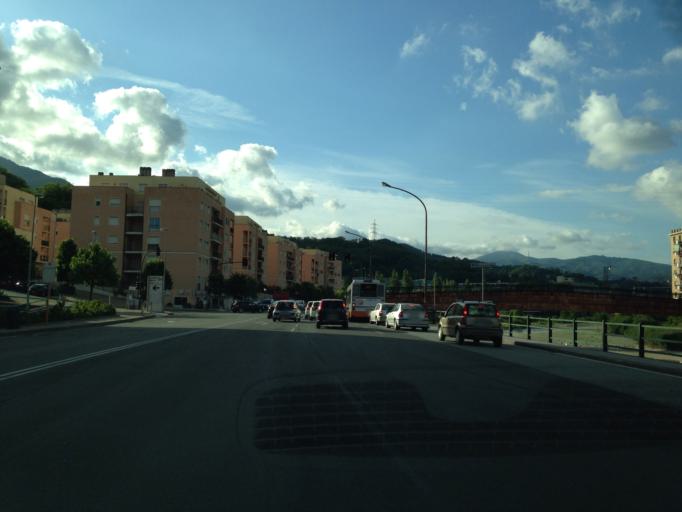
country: IT
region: Liguria
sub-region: Provincia di Genova
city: Manesseno
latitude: 44.4733
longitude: 8.9001
